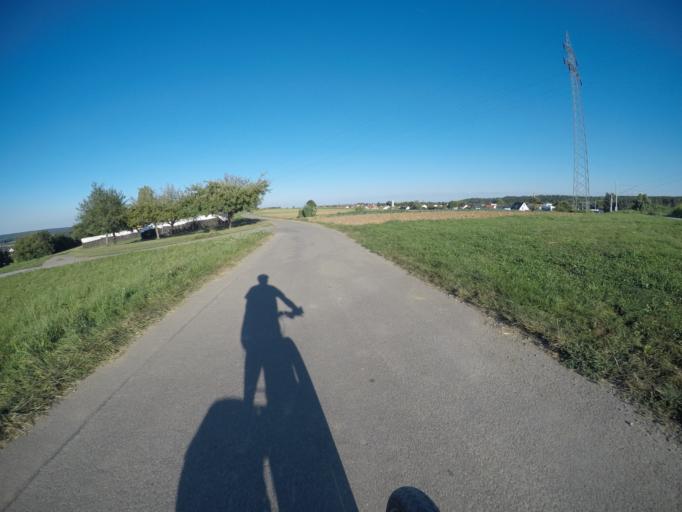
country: DE
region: Baden-Wuerttemberg
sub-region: Regierungsbezirk Stuttgart
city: Weil im Schonbuch
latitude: 48.6231
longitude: 9.0379
